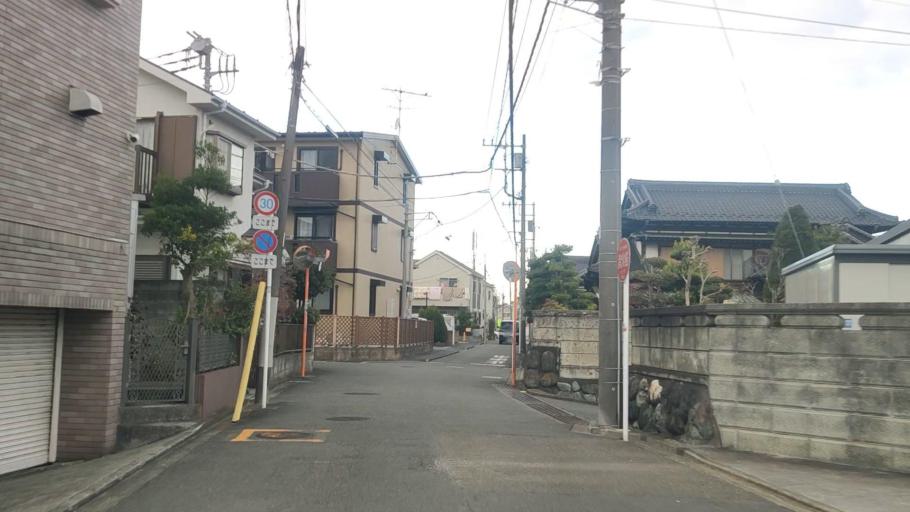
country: JP
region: Kanagawa
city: Minami-rinkan
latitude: 35.4730
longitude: 139.4680
